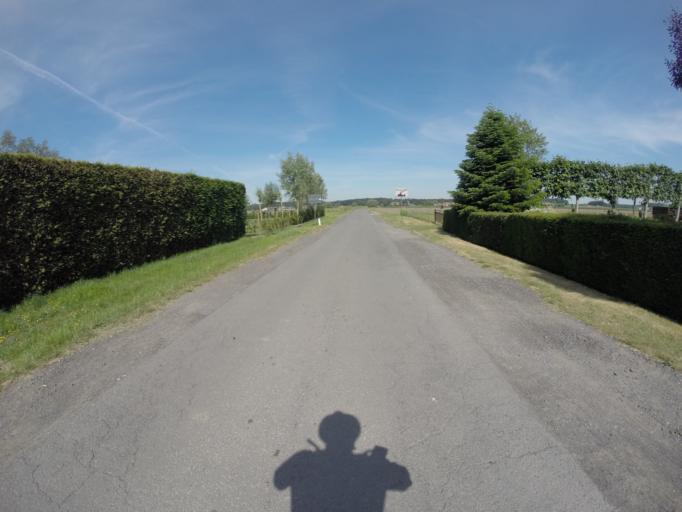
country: BE
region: Flanders
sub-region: Provincie Oost-Vlaanderen
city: Knesselare
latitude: 51.1522
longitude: 3.4099
